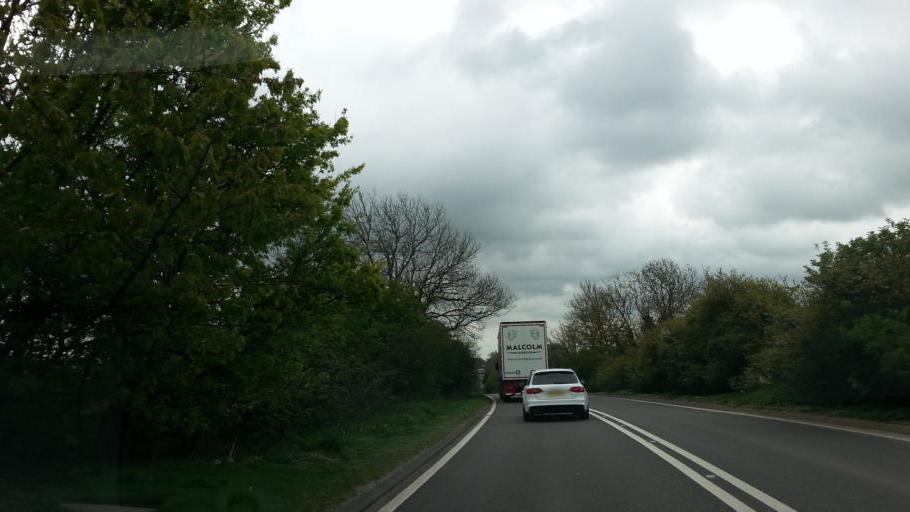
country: GB
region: England
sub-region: Leicestershire
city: Lutterworth
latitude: 52.4129
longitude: -1.2169
